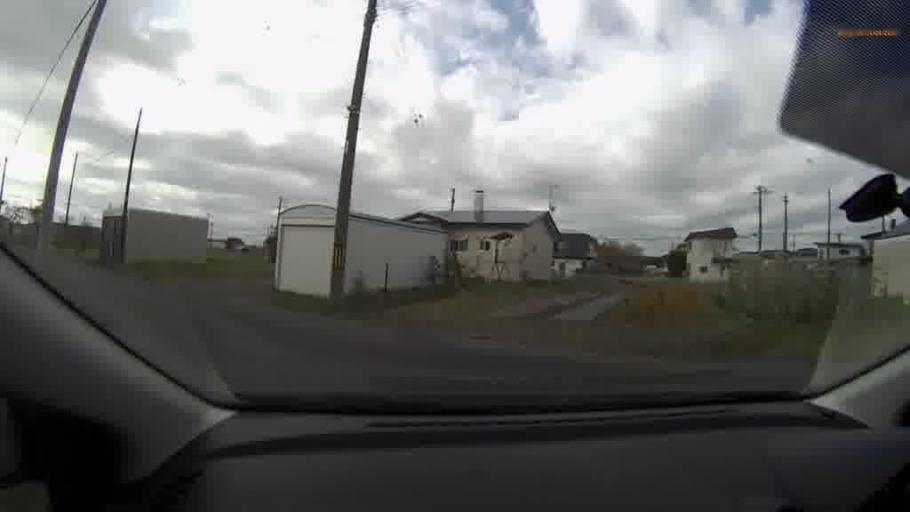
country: JP
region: Hokkaido
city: Kushiro
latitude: 42.9750
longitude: 144.1279
